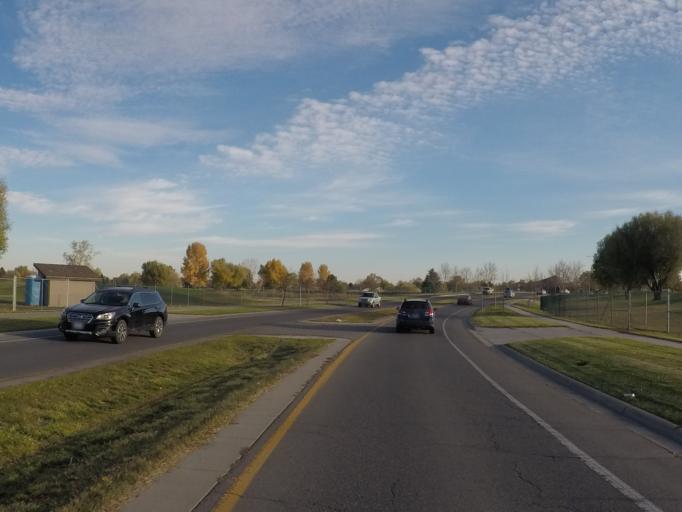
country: US
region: Montana
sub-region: Yellowstone County
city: Billings
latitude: 45.7791
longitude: -108.5979
